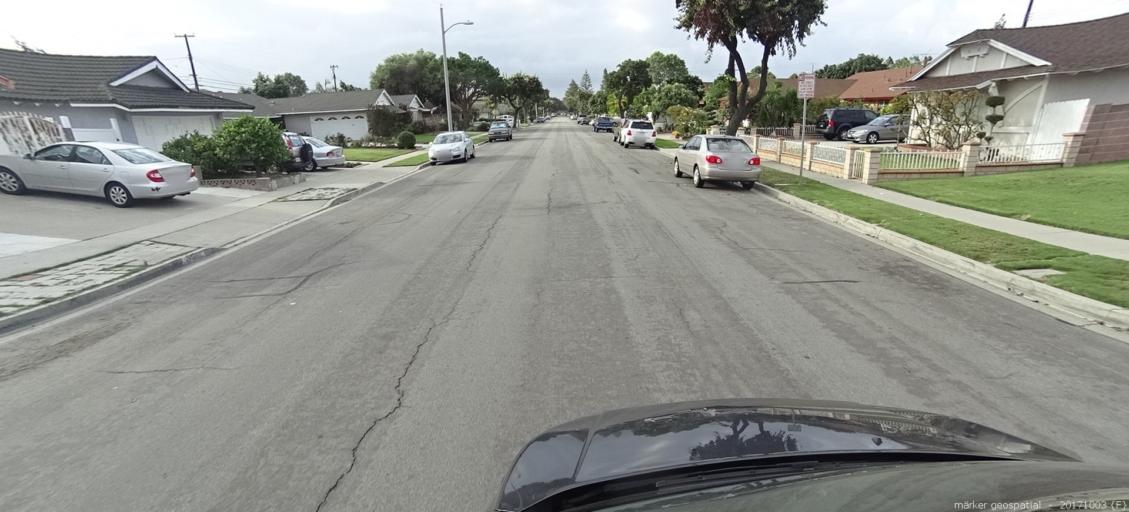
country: US
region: California
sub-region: Orange County
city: Garden Grove
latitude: 33.7445
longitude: -117.9423
